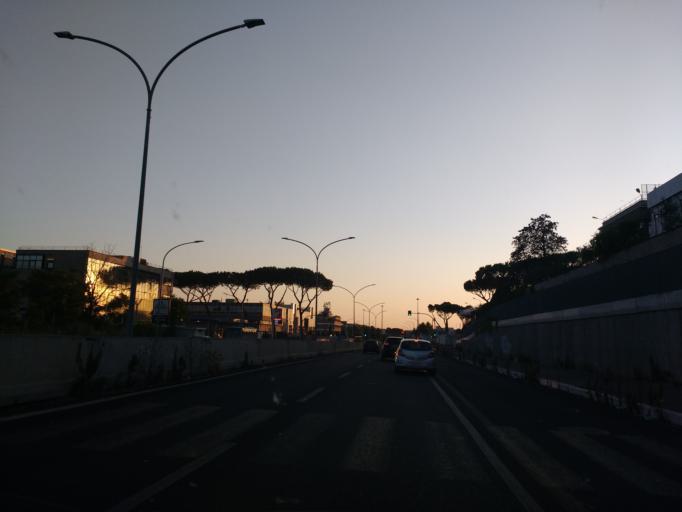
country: IT
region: Latium
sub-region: Citta metropolitana di Roma Capitale
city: Colle Verde
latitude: 41.9344
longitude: 12.6067
